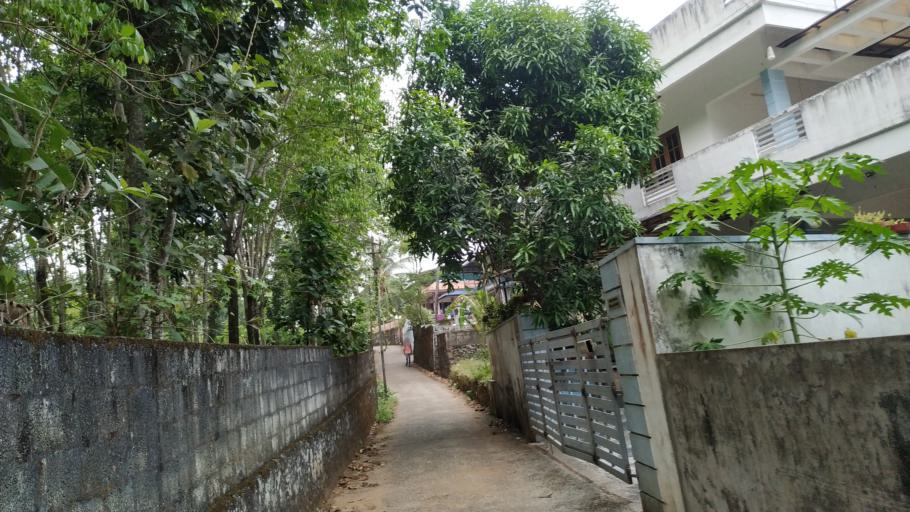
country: IN
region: Kerala
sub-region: Kottayam
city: Lalam
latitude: 9.8424
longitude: 76.7458
